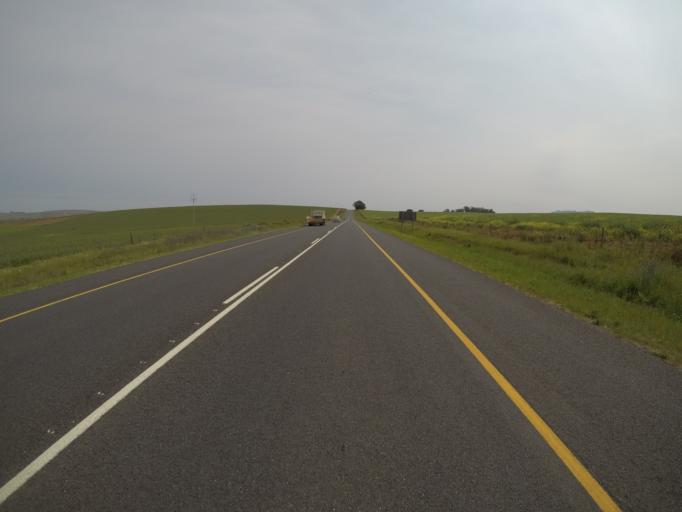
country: ZA
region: Western Cape
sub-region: West Coast District Municipality
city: Malmesbury
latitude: -33.5086
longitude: 18.8425
